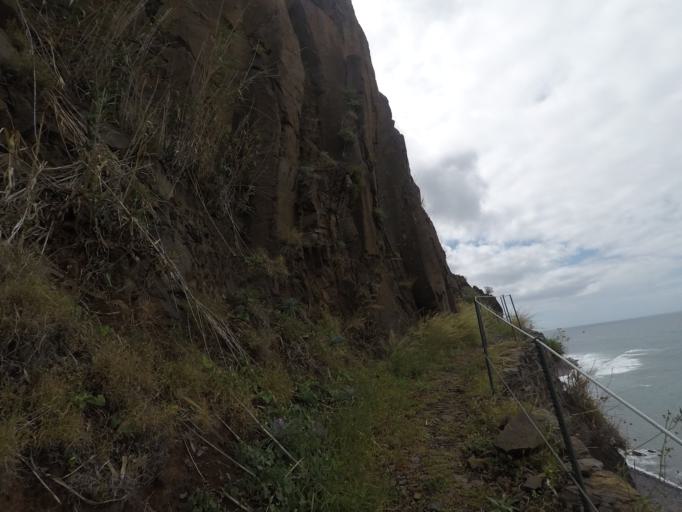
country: PT
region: Madeira
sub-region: Calheta
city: Faja da Ovelha
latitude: 32.7531
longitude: -17.2237
